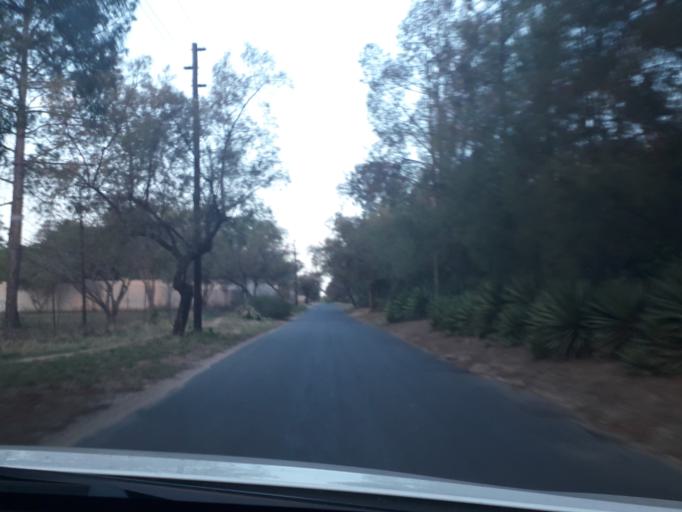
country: ZA
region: Gauteng
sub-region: City of Johannesburg Metropolitan Municipality
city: Diepsloot
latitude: -25.9849
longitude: 28.0523
